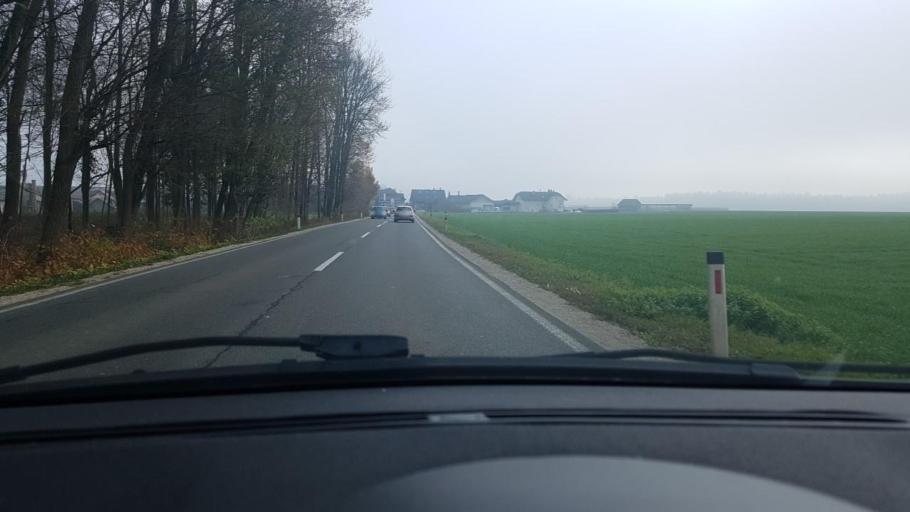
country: SI
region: Vodice
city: Vodice
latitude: 46.2206
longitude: 14.4992
